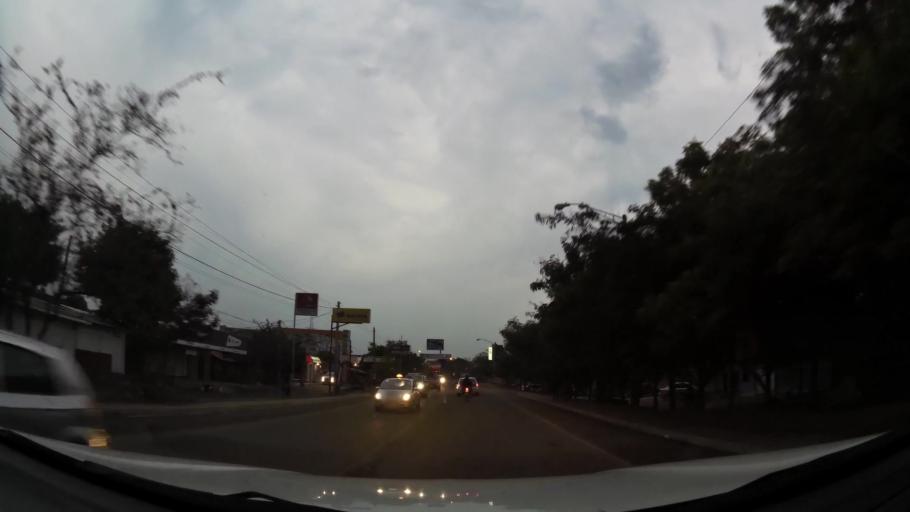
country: NI
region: Esteli
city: Esteli
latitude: 13.0985
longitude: -86.3513
